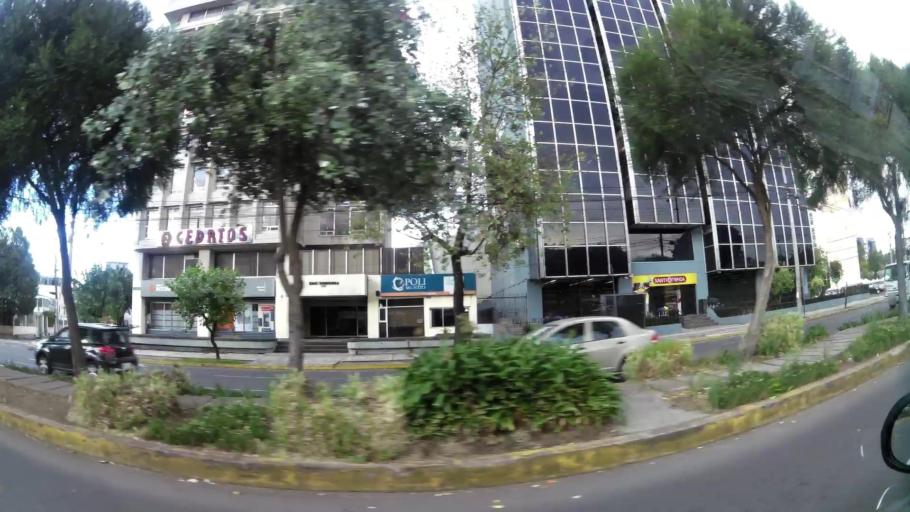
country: EC
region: Pichincha
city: Quito
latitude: -0.1916
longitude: -78.4884
